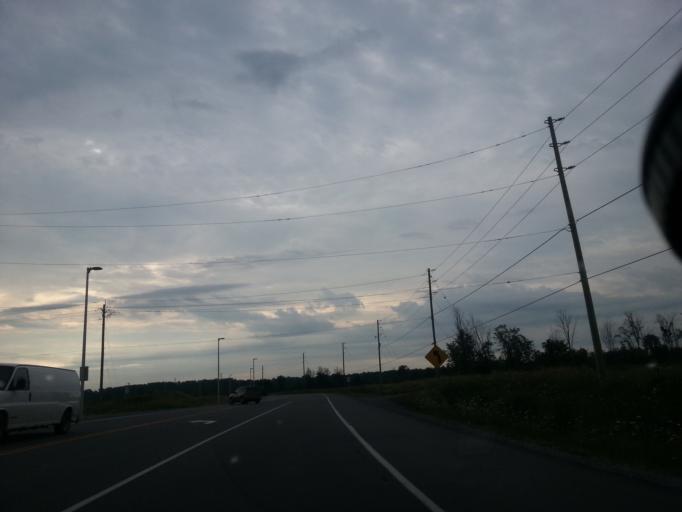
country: CA
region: Ontario
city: Ottawa
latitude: 45.3336
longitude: -75.5906
